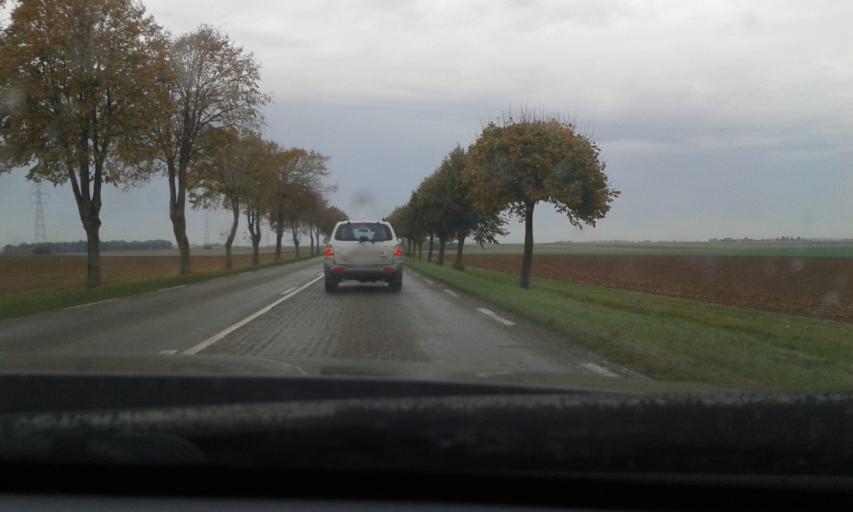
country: FR
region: Centre
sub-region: Departement d'Eure-et-Loir
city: Baigneaux
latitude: 48.1555
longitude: 1.8430
